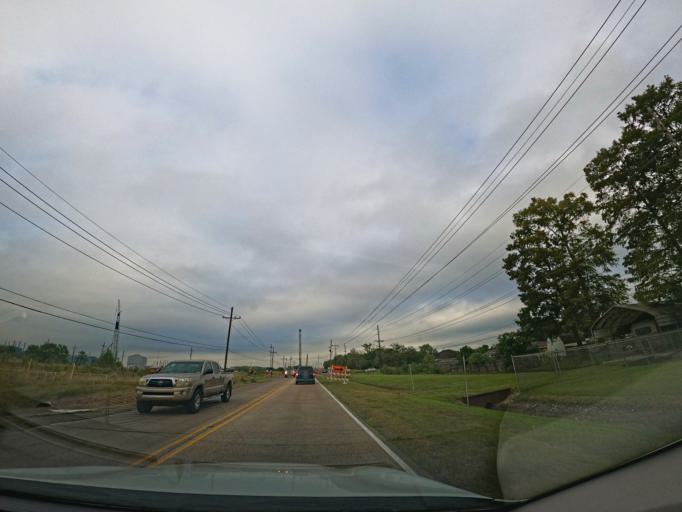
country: US
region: Louisiana
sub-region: Terrebonne Parish
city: Houma
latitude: 29.5721
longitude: -90.6939
